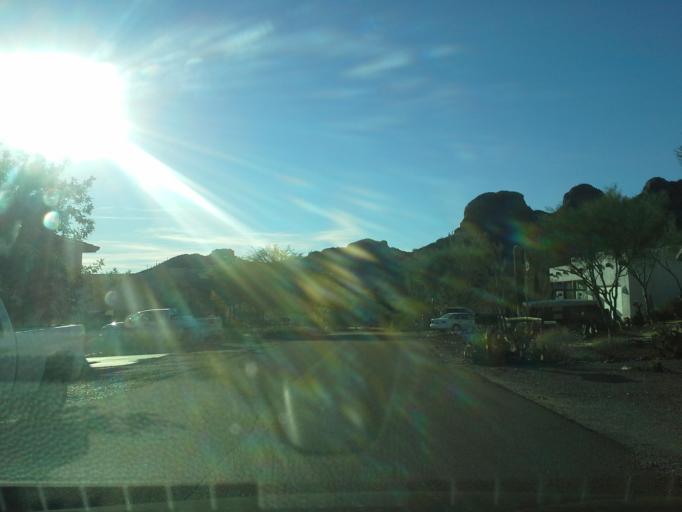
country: US
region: Arizona
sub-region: Pinal County
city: Apache Junction
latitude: 33.3652
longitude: -111.4366
